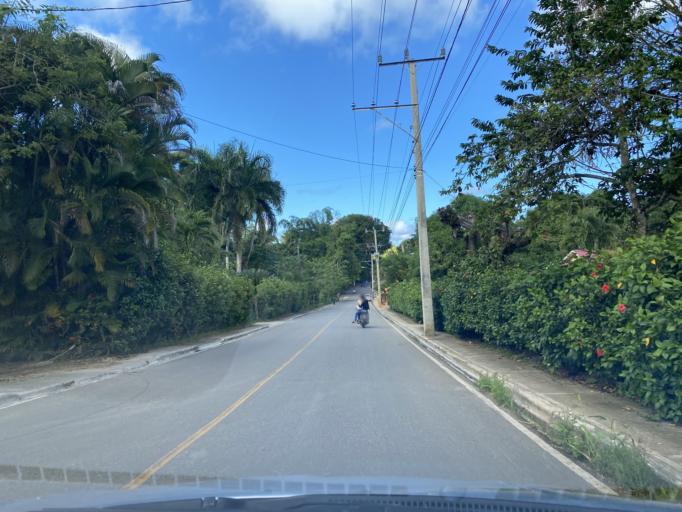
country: DO
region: Samana
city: Las Terrenas
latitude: 19.2897
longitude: -69.5480
